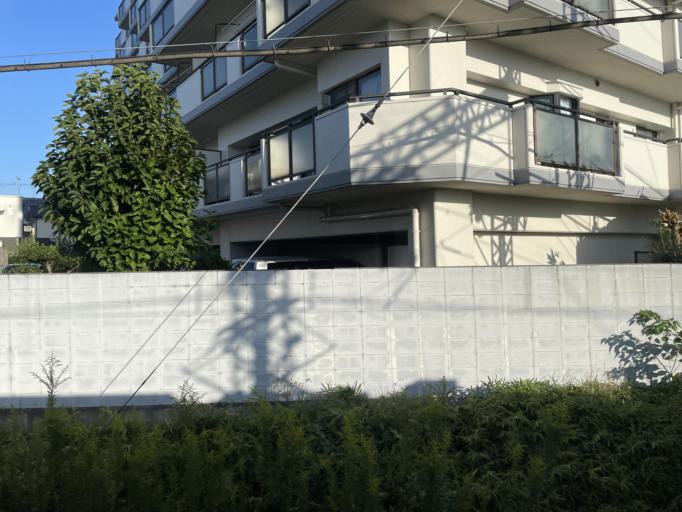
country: JP
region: Osaka
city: Kashihara
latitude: 34.5577
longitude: 135.6137
